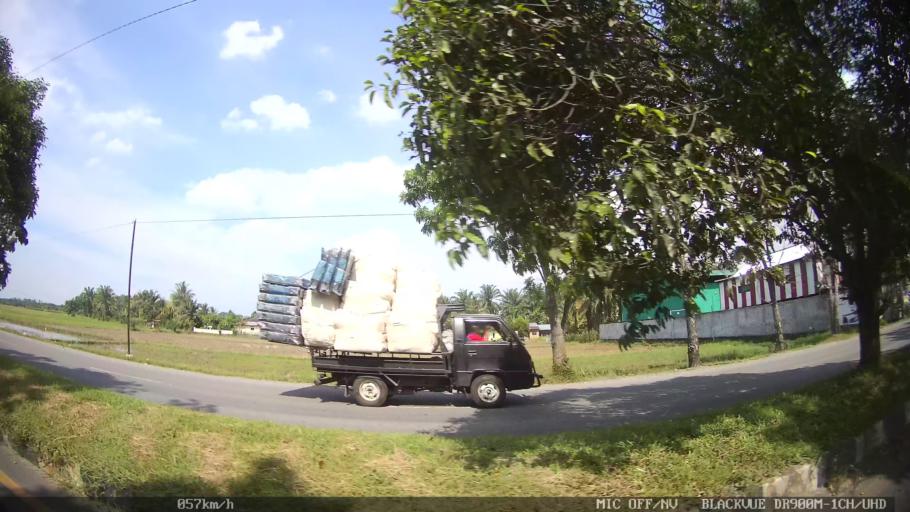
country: ID
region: North Sumatra
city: Binjai
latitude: 3.6145
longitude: 98.5345
